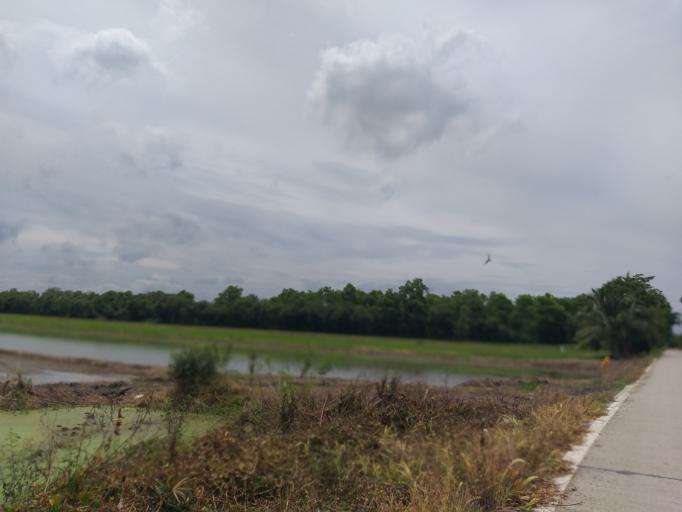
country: TH
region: Pathum Thani
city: Ban Lam Luk Ka
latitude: 14.0306
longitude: 100.8660
